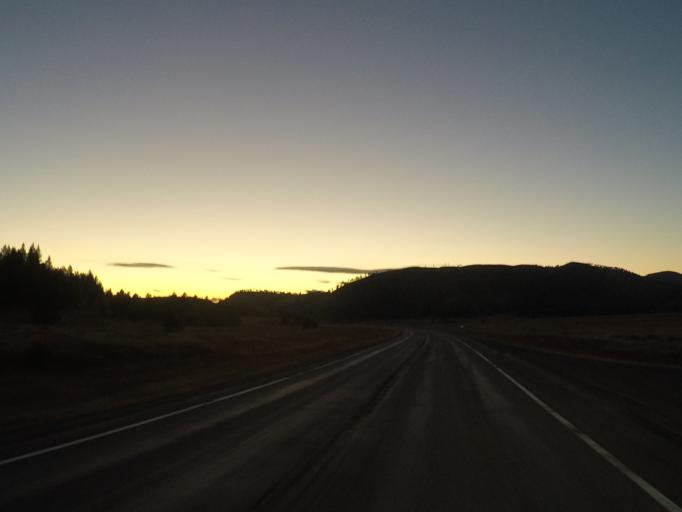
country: US
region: Montana
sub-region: Missoula County
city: Seeley Lake
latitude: 47.0303
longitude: -113.2501
